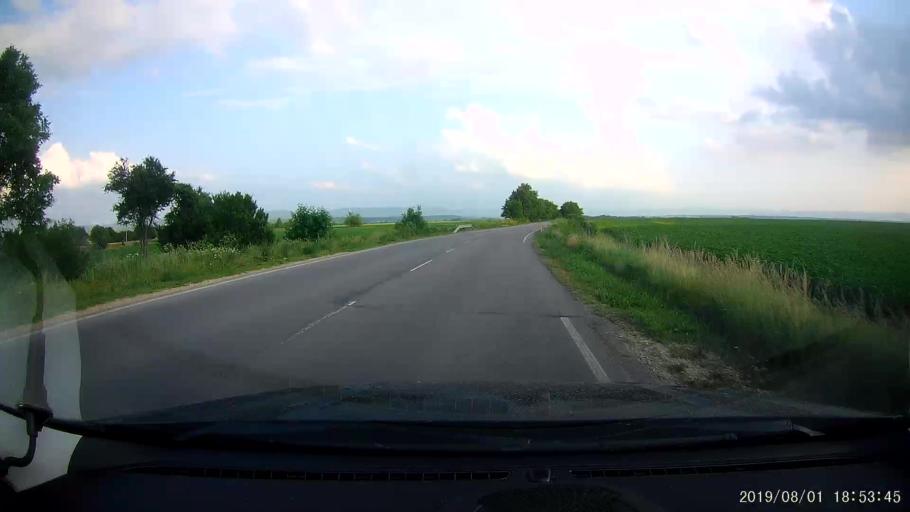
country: BG
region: Shumen
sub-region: Obshtina Shumen
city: Shumen
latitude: 43.2156
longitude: 26.9974
